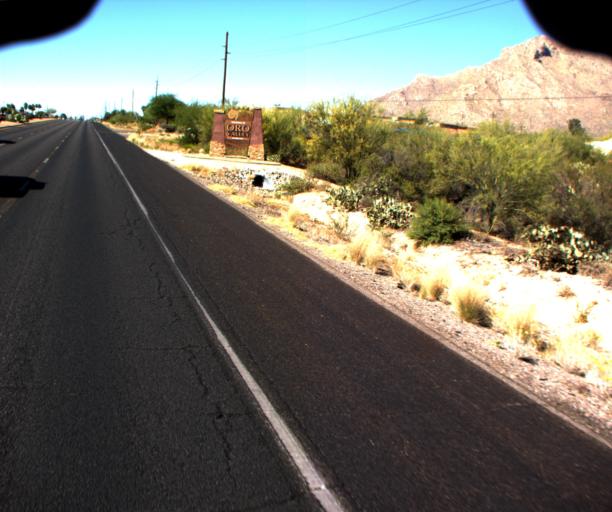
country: US
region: Arizona
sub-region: Pima County
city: Casas Adobes
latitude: 32.3460
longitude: -110.9760
